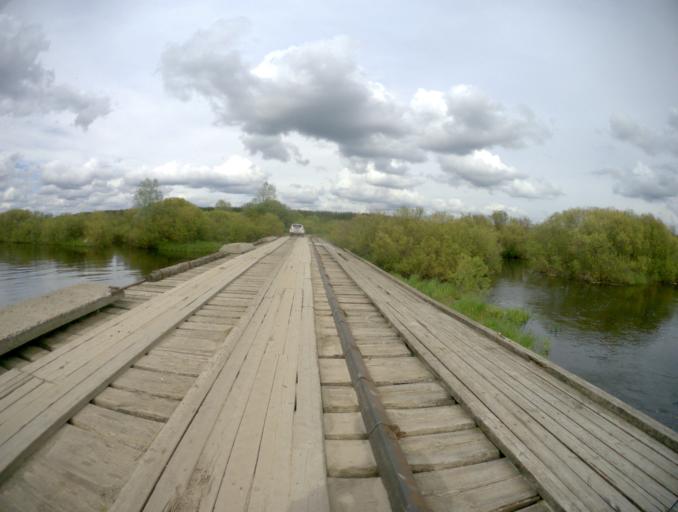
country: RU
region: Rjazan
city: Gus'-Zheleznyy
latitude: 55.0103
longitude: 41.1650
